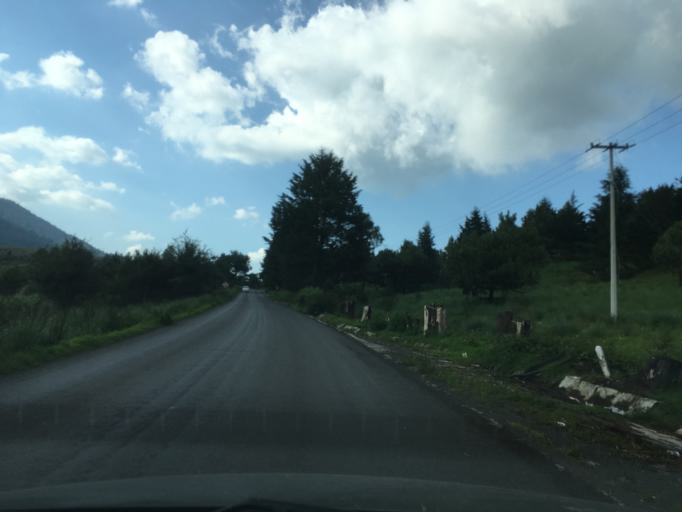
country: MX
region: Michoacan
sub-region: Nahuatzen
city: Sevina
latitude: 19.6140
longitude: -101.9337
